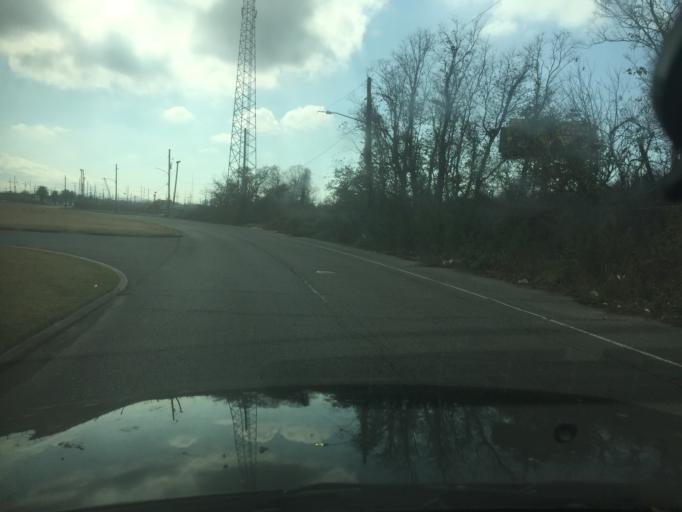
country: US
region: Louisiana
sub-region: Orleans Parish
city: New Orleans
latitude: 29.9987
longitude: -90.0417
